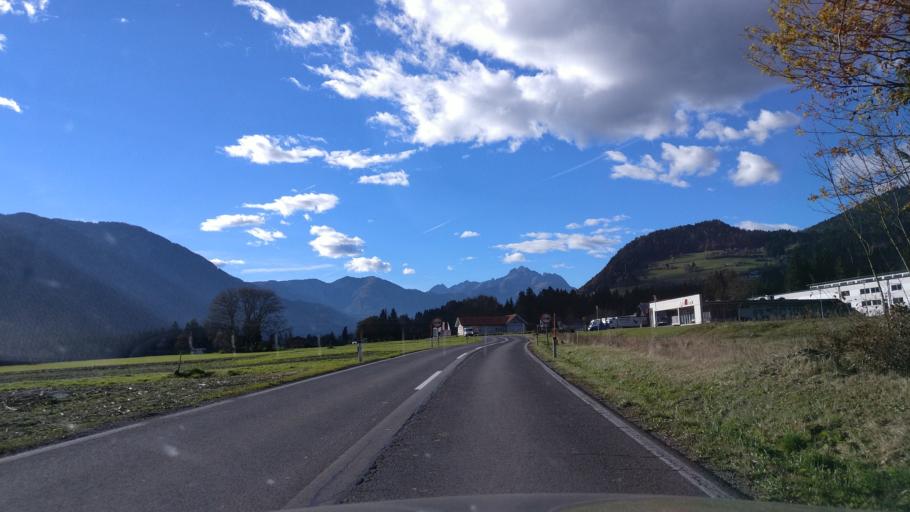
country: AT
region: Carinthia
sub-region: Politischer Bezirk Spittal an der Drau
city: Dellach im Drautal
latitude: 46.7384
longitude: 13.0955
